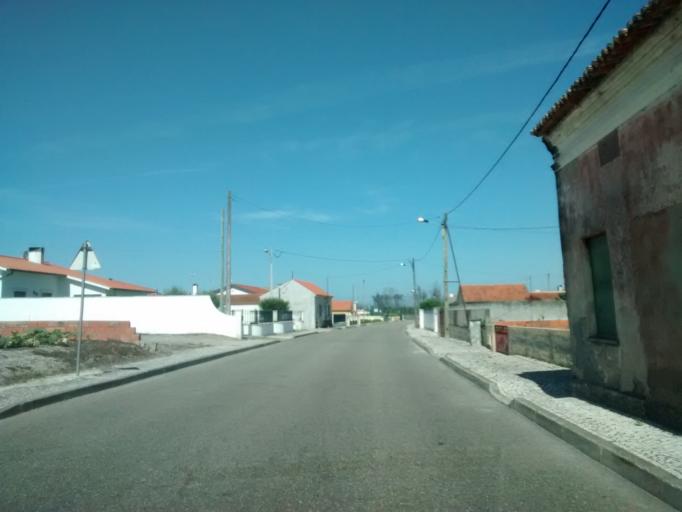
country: PT
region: Coimbra
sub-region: Mira
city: Mira
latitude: 40.4279
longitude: -8.6925
